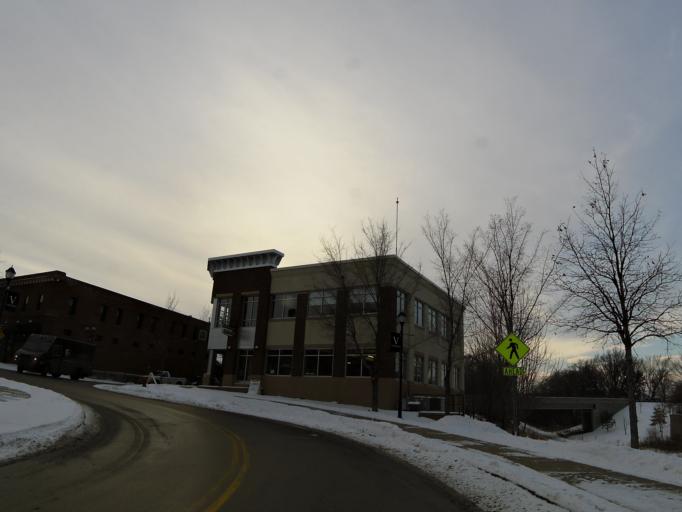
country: US
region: Minnesota
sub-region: Carver County
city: Victoria
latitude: 44.8603
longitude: -93.6617
